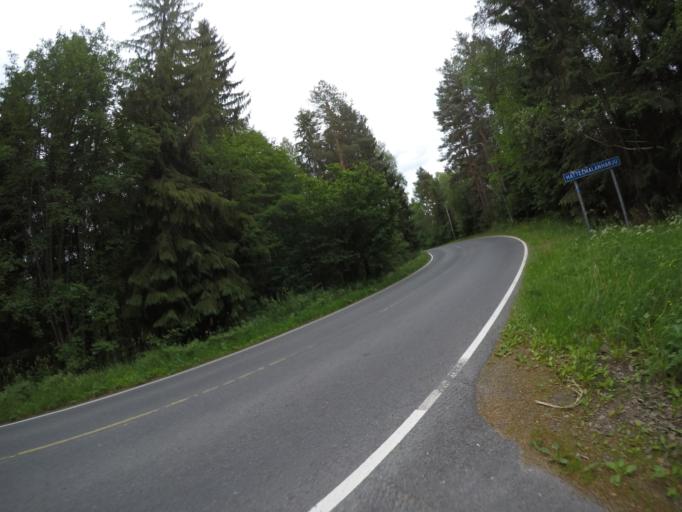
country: FI
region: Haeme
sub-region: Haemeenlinna
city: Haemeenlinna
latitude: 60.9779
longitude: 24.4531
